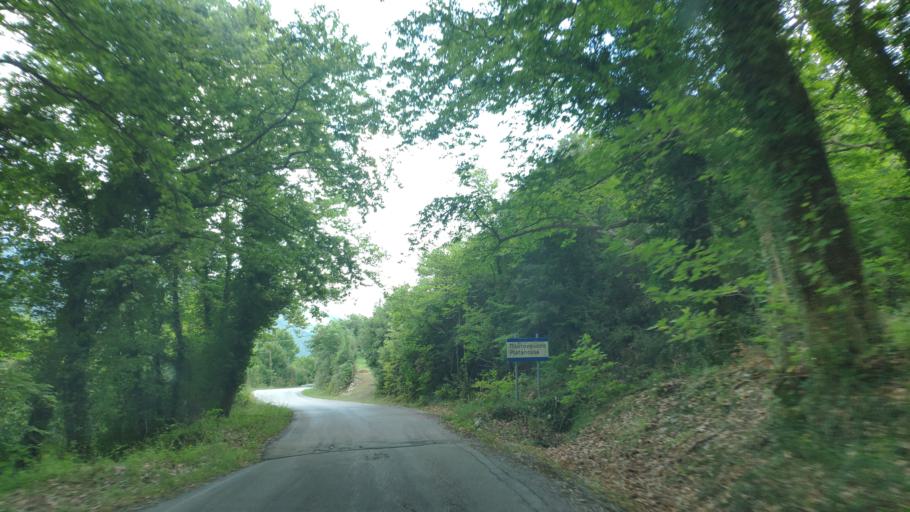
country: GR
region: Epirus
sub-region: Nomos Artas
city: Agios Dimitrios
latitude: 39.4361
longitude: 21.0146
